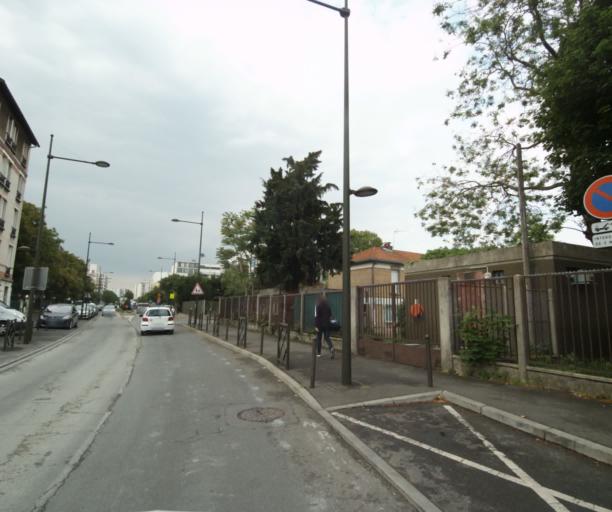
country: FR
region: Ile-de-France
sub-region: Departement du Val-d'Oise
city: Argenteuil
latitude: 48.9437
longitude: 2.2346
